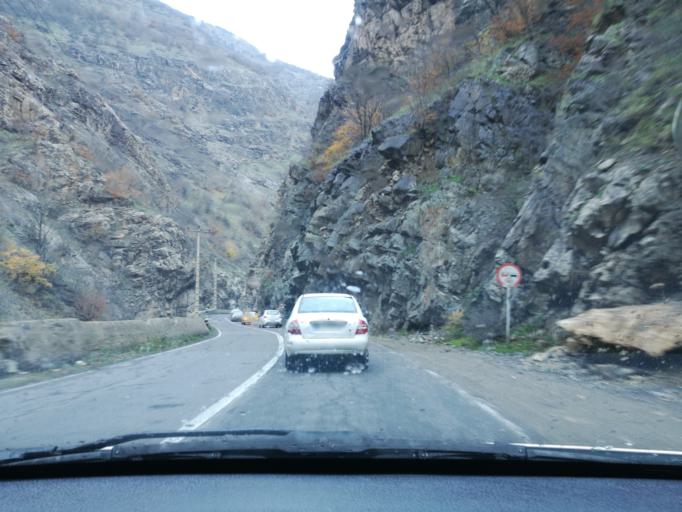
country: IR
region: Mazandaran
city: Chalus
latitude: 36.2903
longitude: 51.2393
